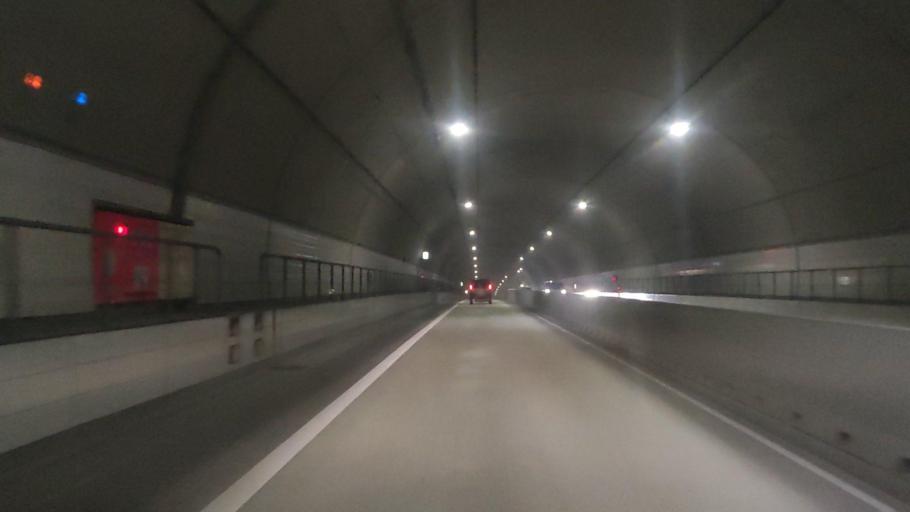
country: JP
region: Kumamoto
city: Ozu
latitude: 32.9093
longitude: 130.9669
